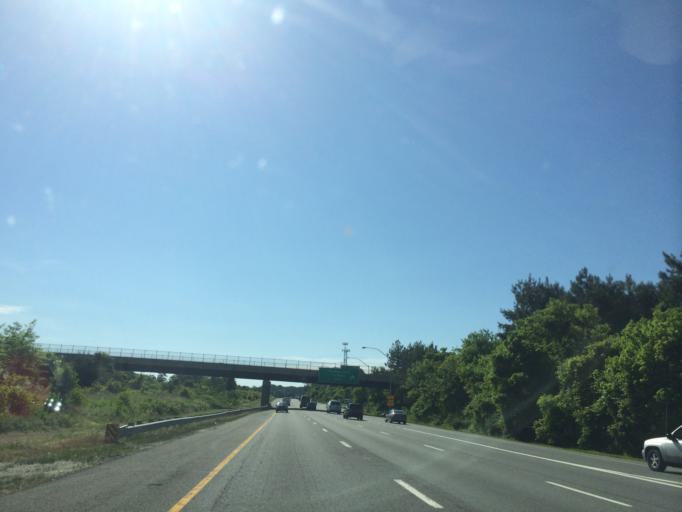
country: US
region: Maryland
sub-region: Howard County
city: Riverside
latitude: 39.1734
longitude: -76.8523
